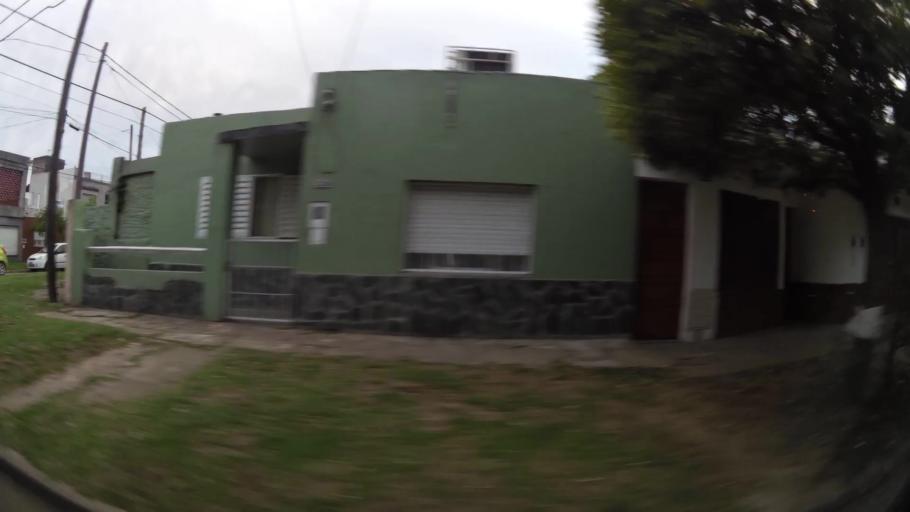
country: AR
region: Santa Fe
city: Granadero Baigorria
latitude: -32.8843
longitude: -60.6981
